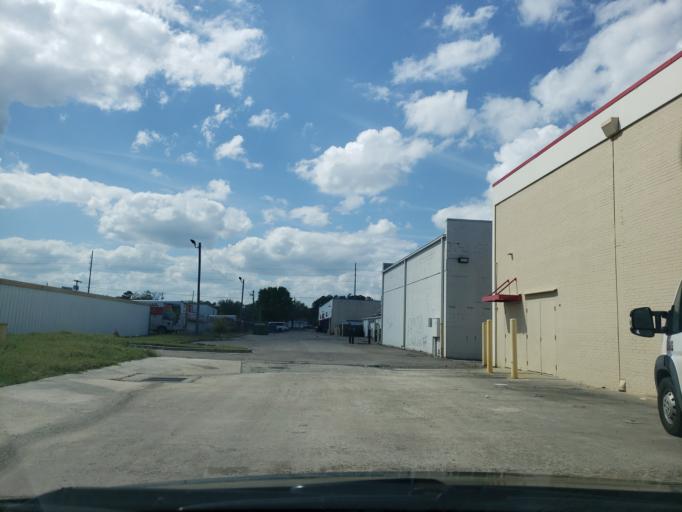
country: US
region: Georgia
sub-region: Chatham County
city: Montgomery
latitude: 31.9974
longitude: -81.1256
